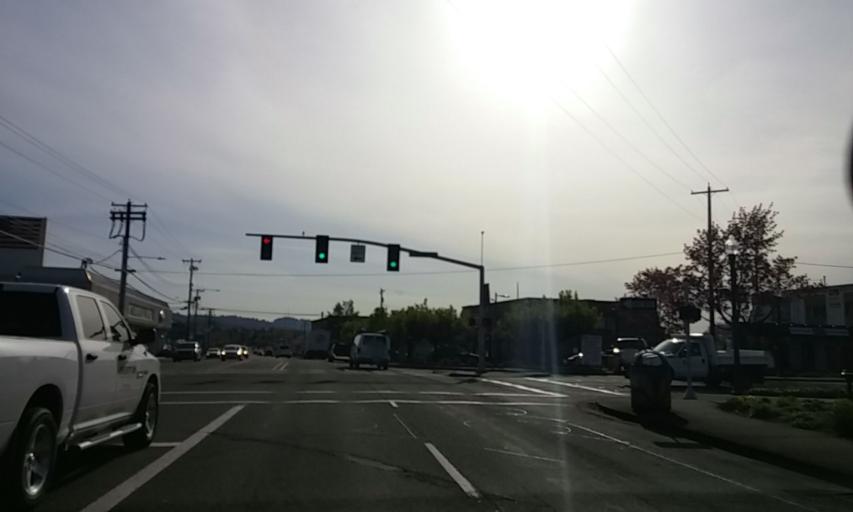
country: US
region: Oregon
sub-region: Washington County
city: Beaverton
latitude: 45.4884
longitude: -122.8045
